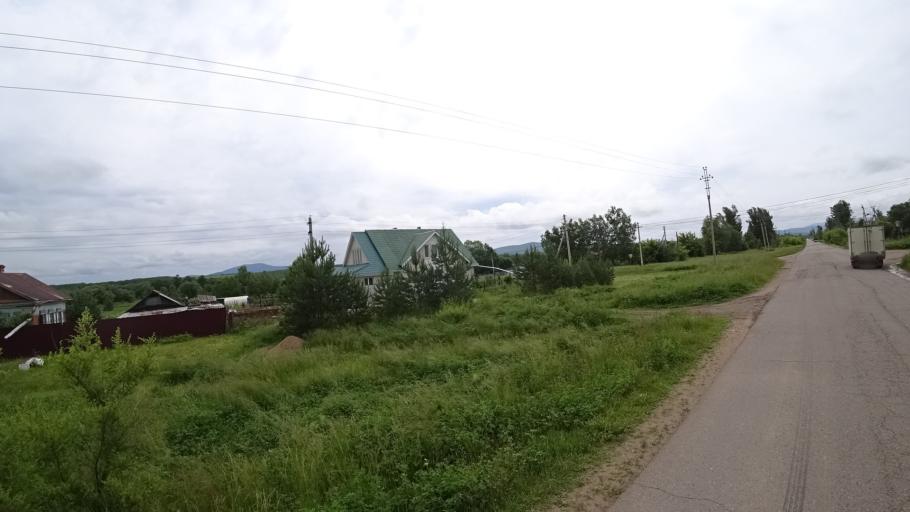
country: RU
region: Primorskiy
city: Novosysoyevka
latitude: 44.2413
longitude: 133.3681
